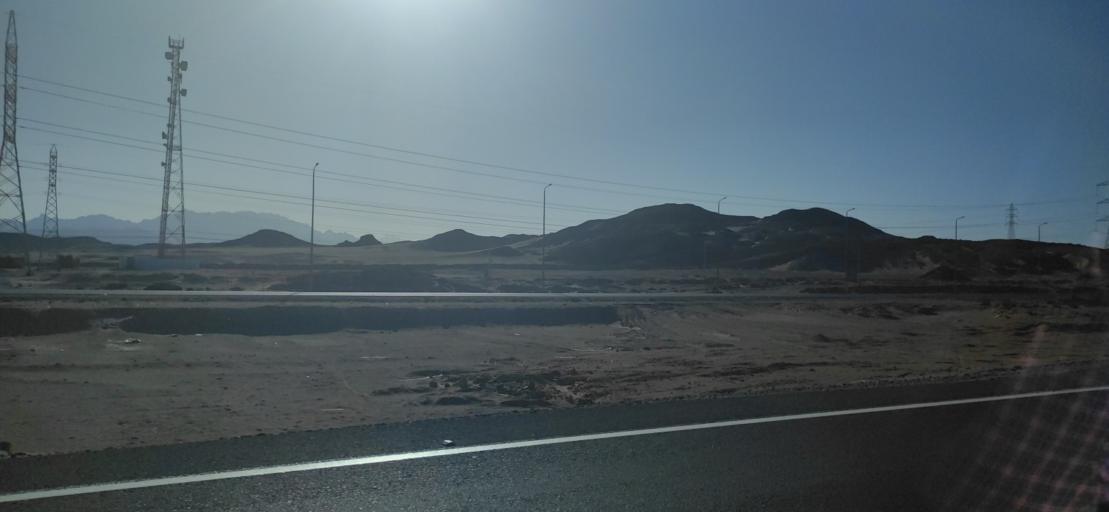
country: EG
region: Red Sea
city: Makadi Bay
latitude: 26.8710
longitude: 33.9097
